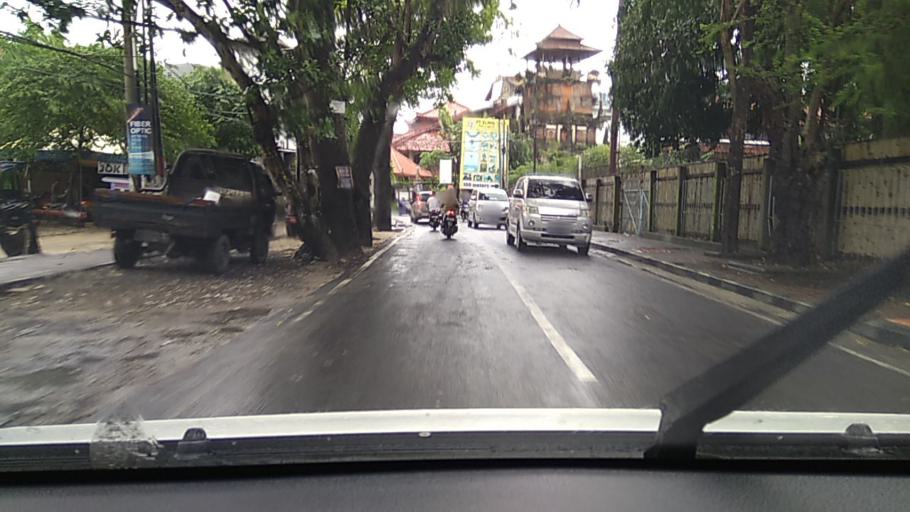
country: ID
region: Bali
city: Bualu
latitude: -8.7879
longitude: 115.2261
